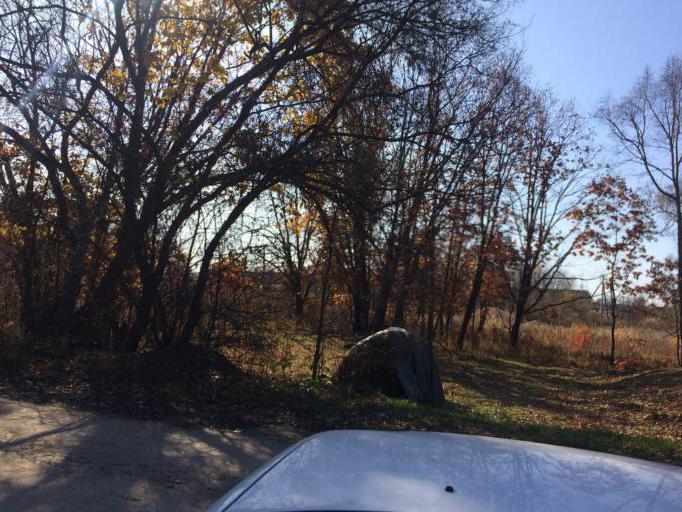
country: RU
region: Primorskiy
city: Dal'nerechensk
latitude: 45.9125
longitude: 133.8068
